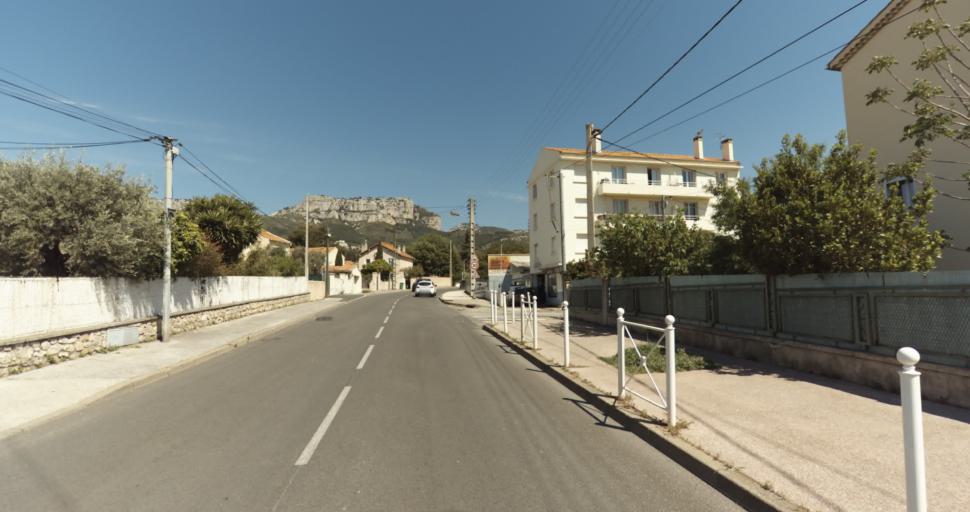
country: FR
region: Provence-Alpes-Cote d'Azur
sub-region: Departement du Var
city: Toulon
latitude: 43.1428
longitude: 5.9018
